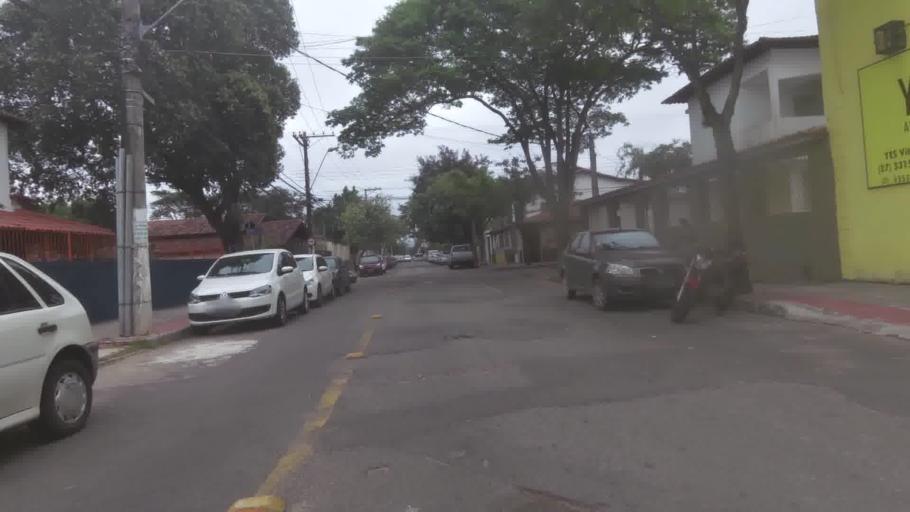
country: BR
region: Espirito Santo
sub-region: Vila Velha
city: Vila Velha
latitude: -20.2571
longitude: -40.2912
